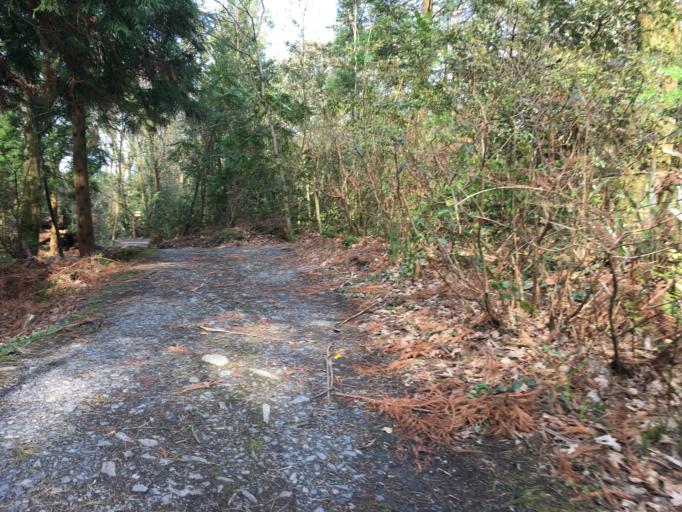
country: GB
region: Wales
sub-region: Gwynedd
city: Porthmadog
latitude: 52.9129
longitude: -4.1049
